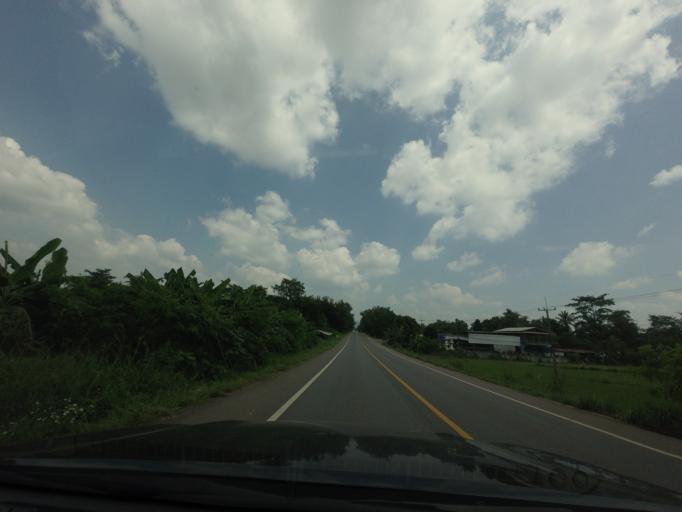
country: TH
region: Phitsanulok
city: Chat Trakan
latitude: 17.3065
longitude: 100.4691
